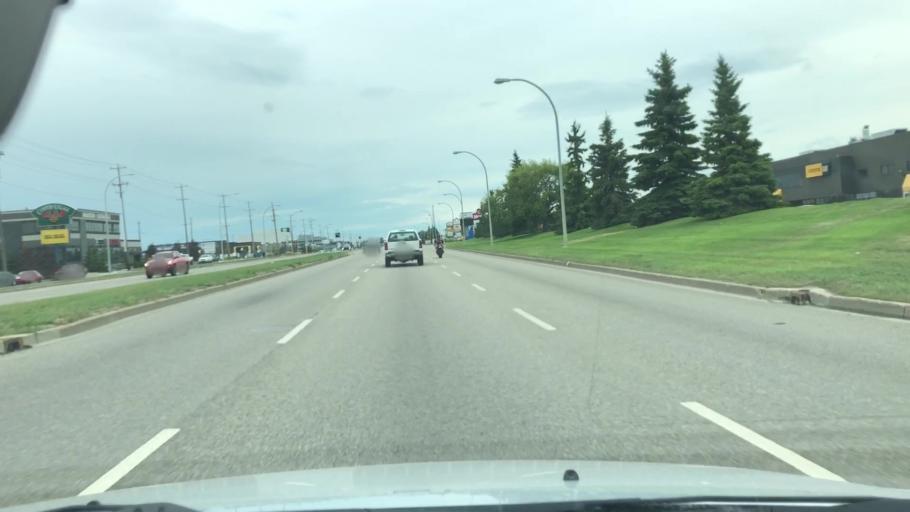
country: CA
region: Alberta
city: St. Albert
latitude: 53.5580
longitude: -113.6155
